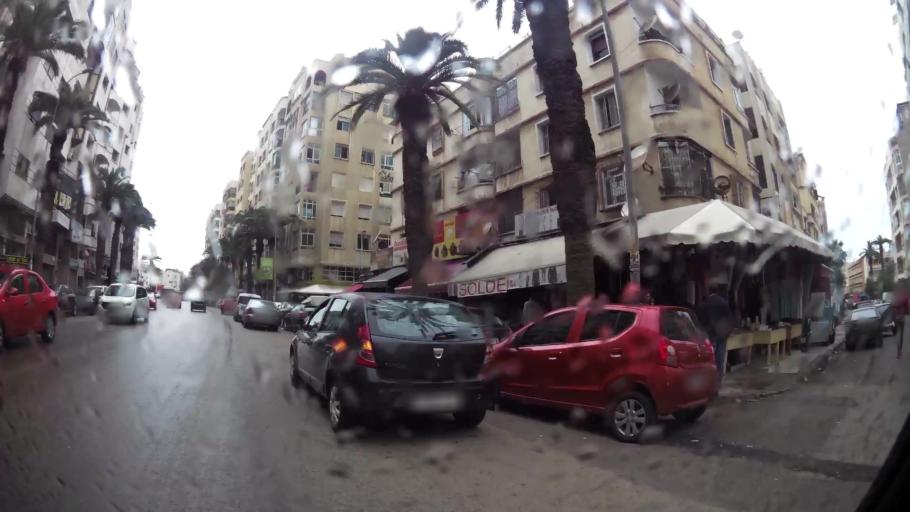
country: MA
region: Grand Casablanca
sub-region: Casablanca
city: Casablanca
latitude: 33.6007
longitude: -7.6370
